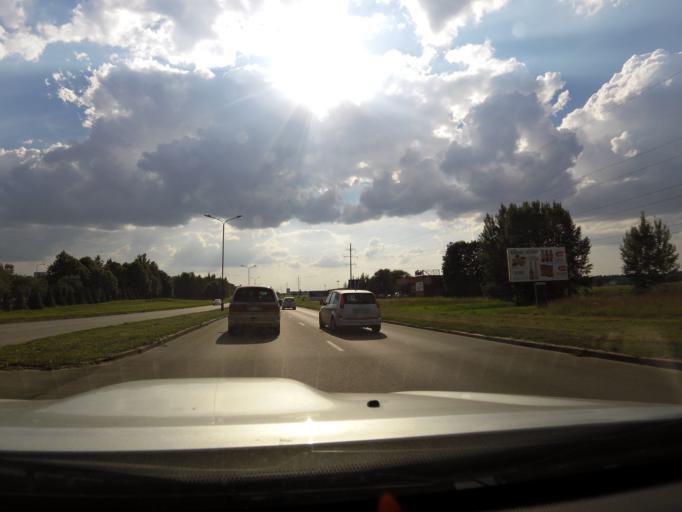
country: LT
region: Siauliu apskritis
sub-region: Siauliai
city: Siauliai
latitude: 55.9227
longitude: 23.2703
